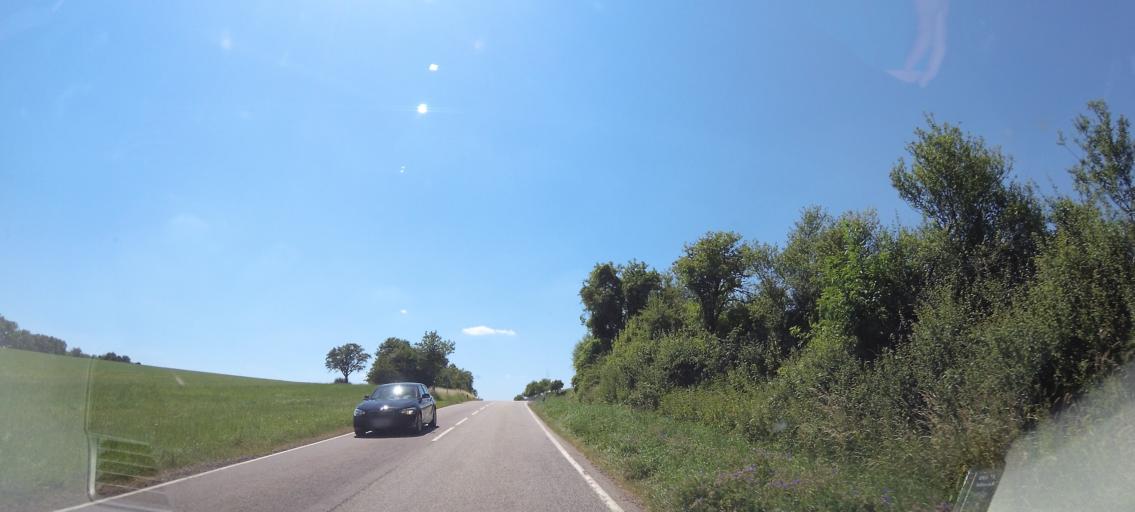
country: DE
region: Saarland
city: Merzig
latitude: 49.4384
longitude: 6.5821
